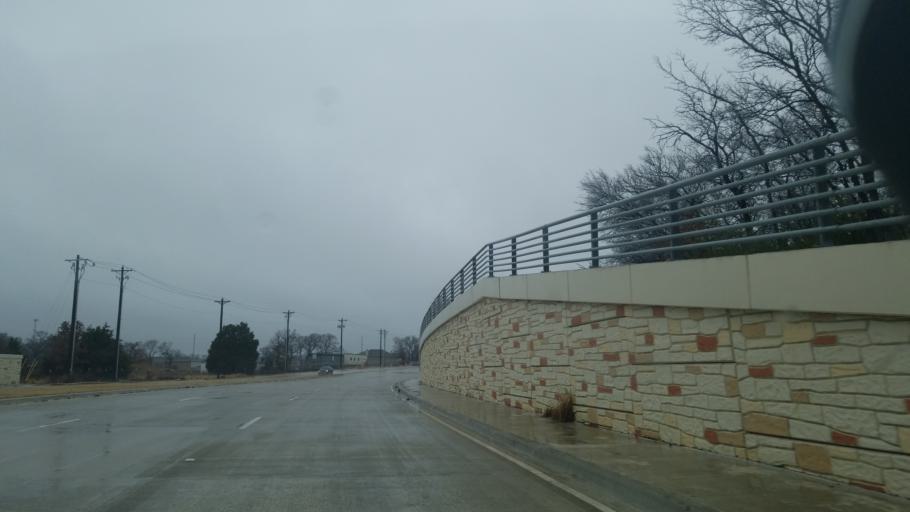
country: US
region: Texas
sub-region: Denton County
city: Corinth
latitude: 33.1444
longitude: -97.0967
